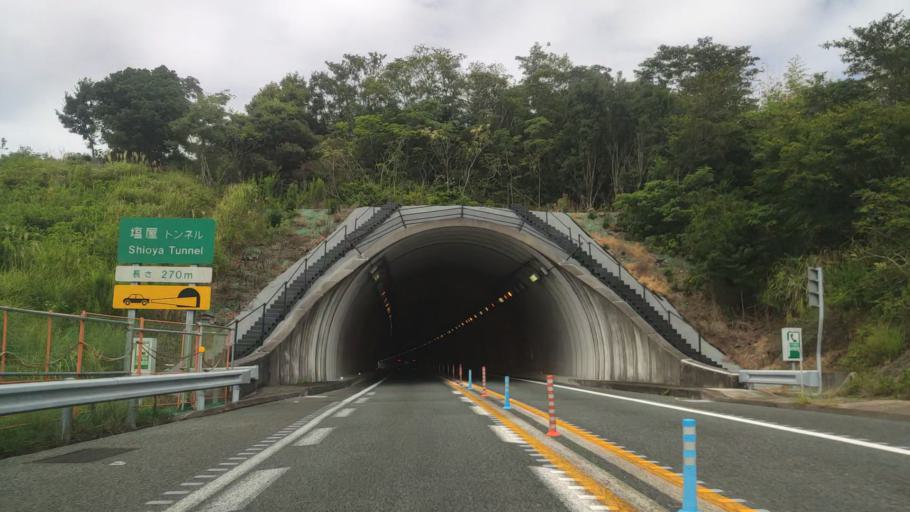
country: JP
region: Wakayama
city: Gobo
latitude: 33.8759
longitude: 135.1872
